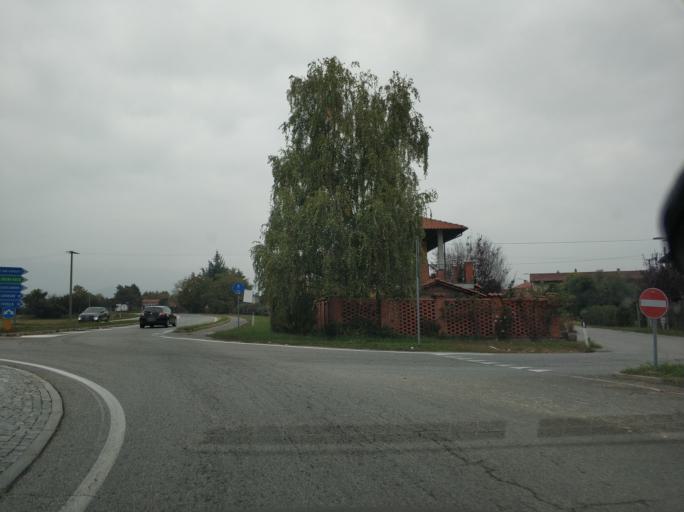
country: IT
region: Piedmont
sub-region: Provincia di Torino
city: Ozegna
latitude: 45.3466
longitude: 7.7421
